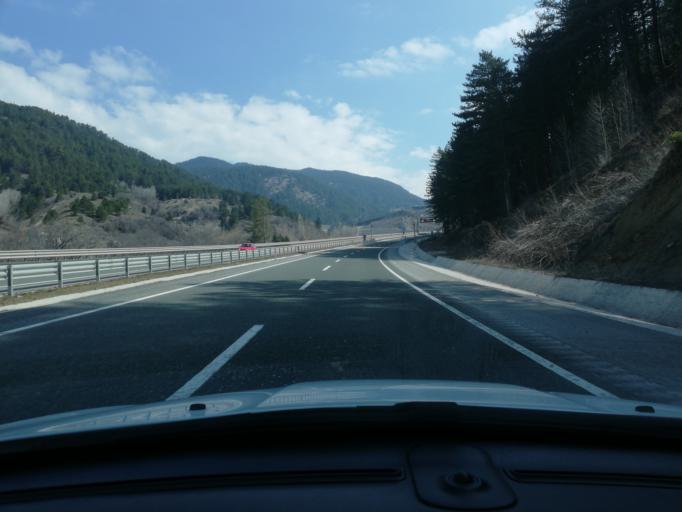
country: TR
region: Cankiri
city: Ilgaz
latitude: 41.0303
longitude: 33.7376
